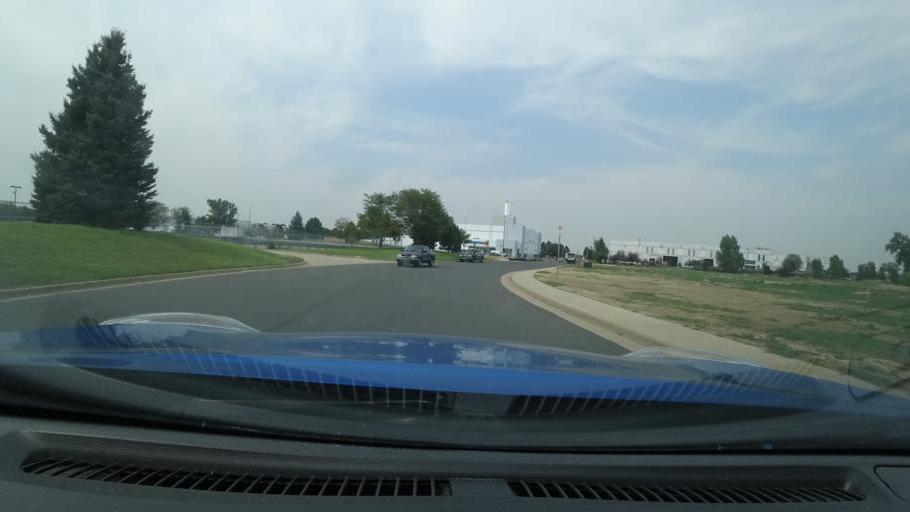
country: US
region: Colorado
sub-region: Adams County
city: Aurora
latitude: 39.7564
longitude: -104.7759
